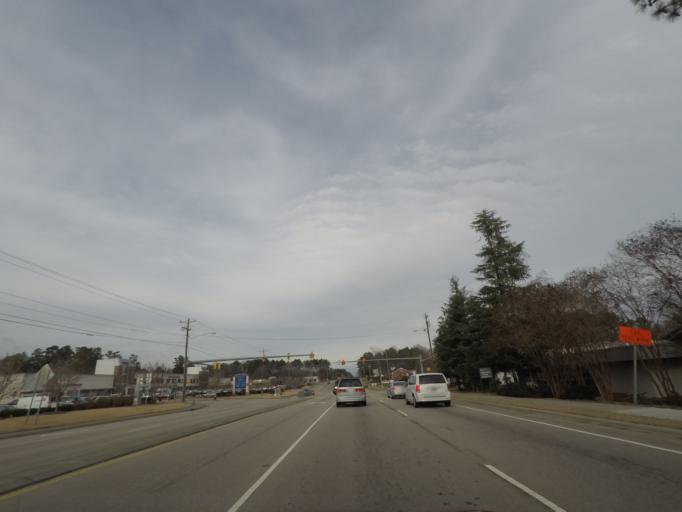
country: US
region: North Carolina
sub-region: Durham County
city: Durham
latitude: 36.0306
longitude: -78.9357
